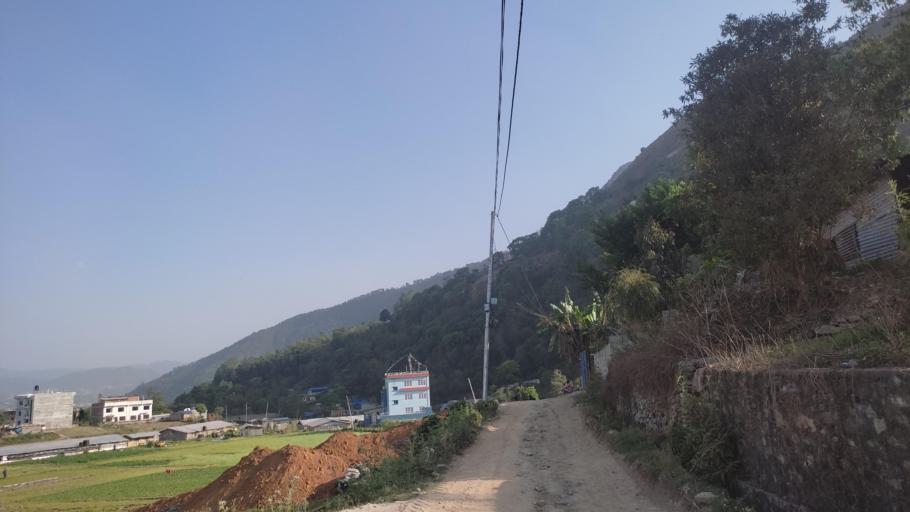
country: NP
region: Central Region
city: Kirtipur
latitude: 27.6574
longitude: 85.2712
